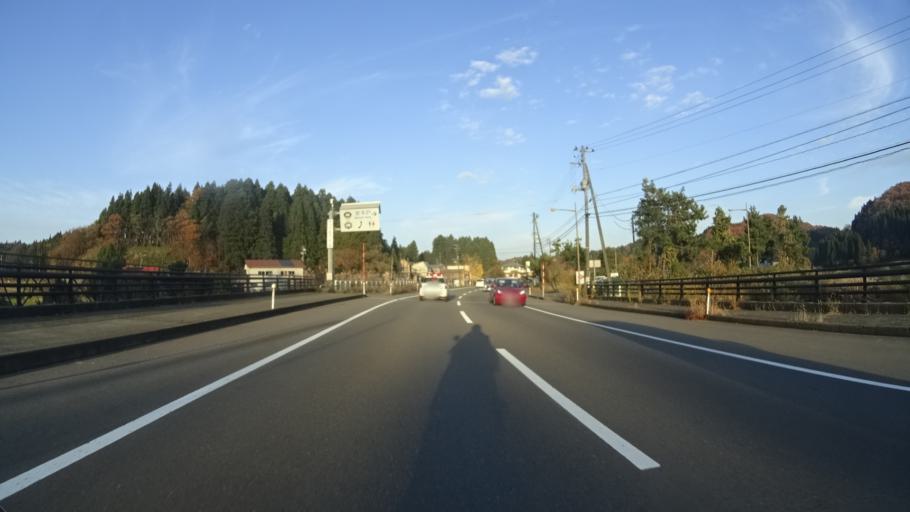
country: JP
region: Niigata
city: Nagaoka
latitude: 37.4363
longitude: 138.7312
